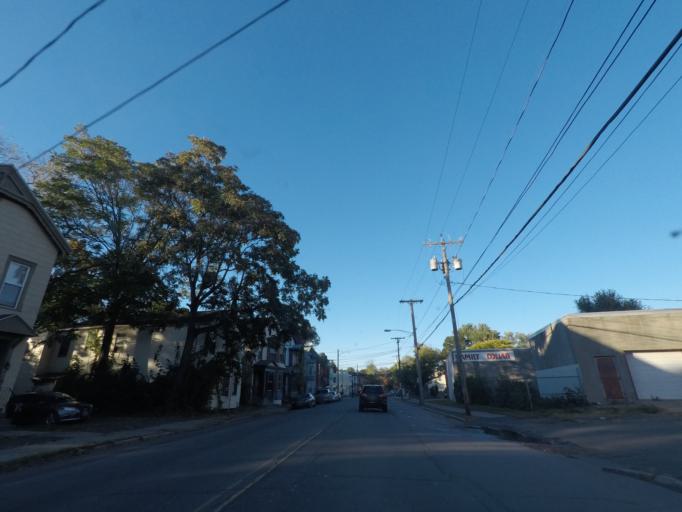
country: US
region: New York
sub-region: Albany County
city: Green Island
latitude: 42.7555
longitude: -73.6825
